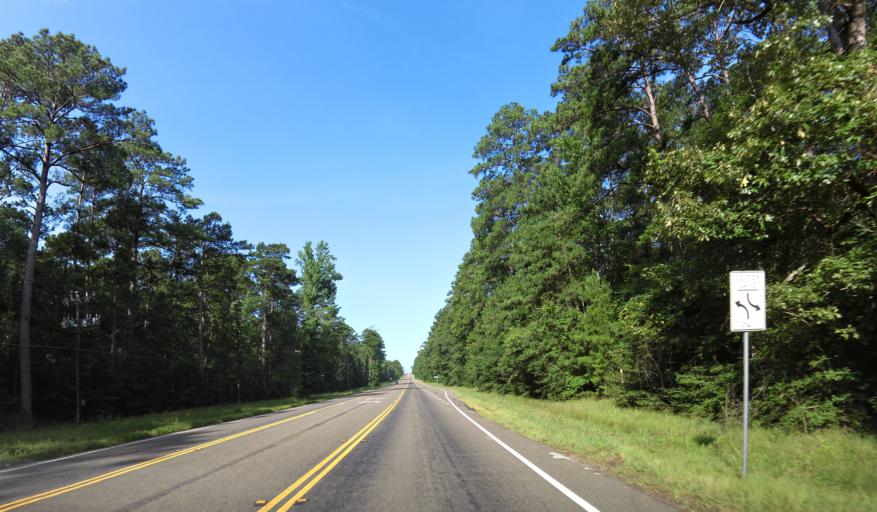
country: US
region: Texas
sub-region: Angelina County
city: Huntington
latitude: 31.1773
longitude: -94.3808
